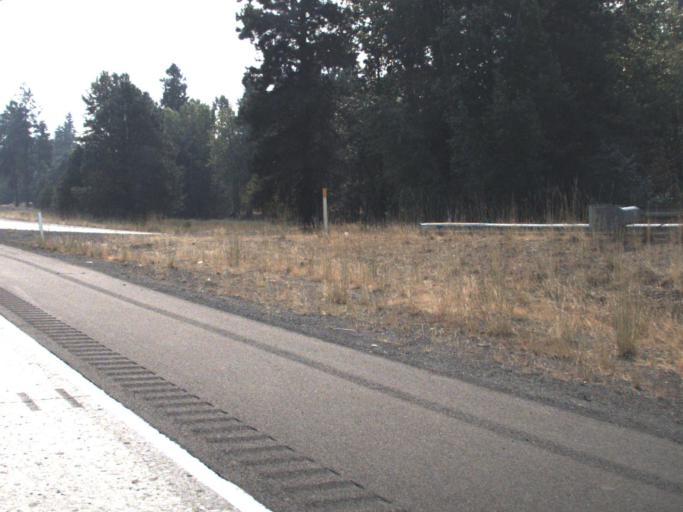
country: US
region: Washington
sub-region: Kittitas County
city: Cle Elum
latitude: 47.1905
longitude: -120.9340
